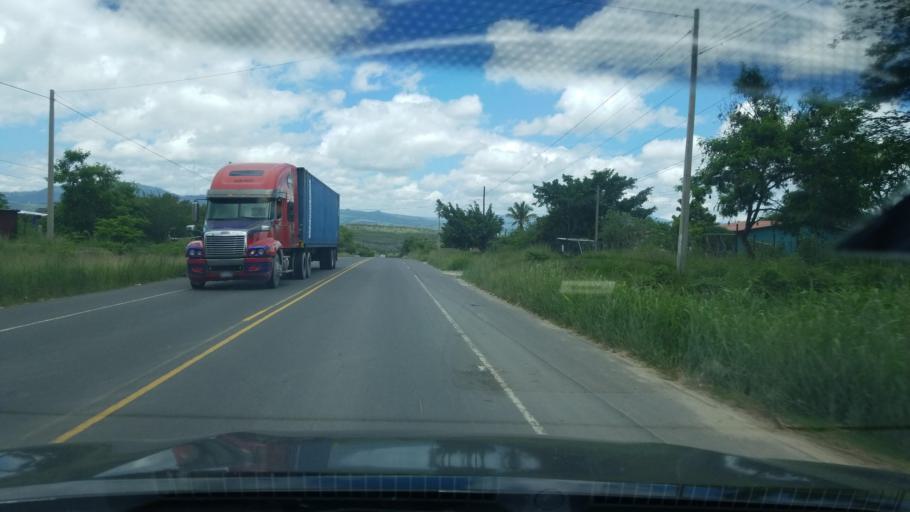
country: HN
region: Francisco Morazan
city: Cofradia
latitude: 14.3158
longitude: -87.2134
